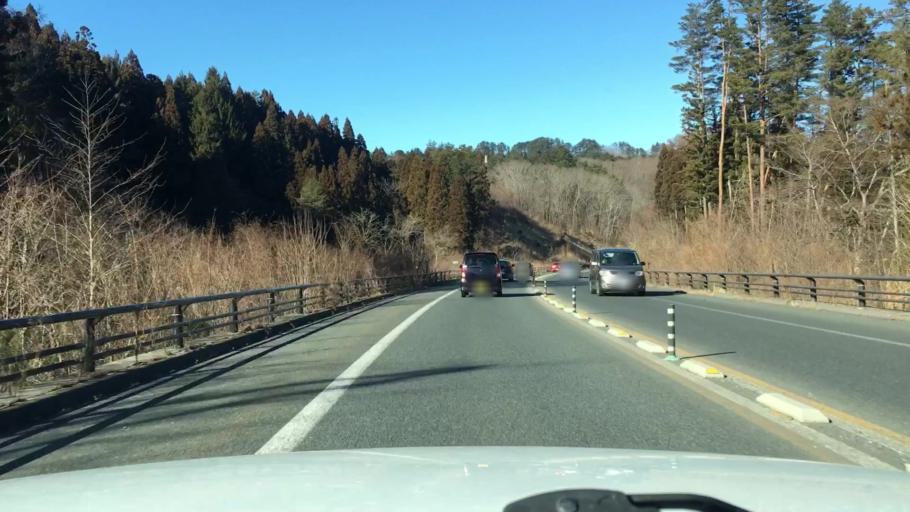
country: JP
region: Iwate
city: Miyako
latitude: 39.6037
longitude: 141.9318
